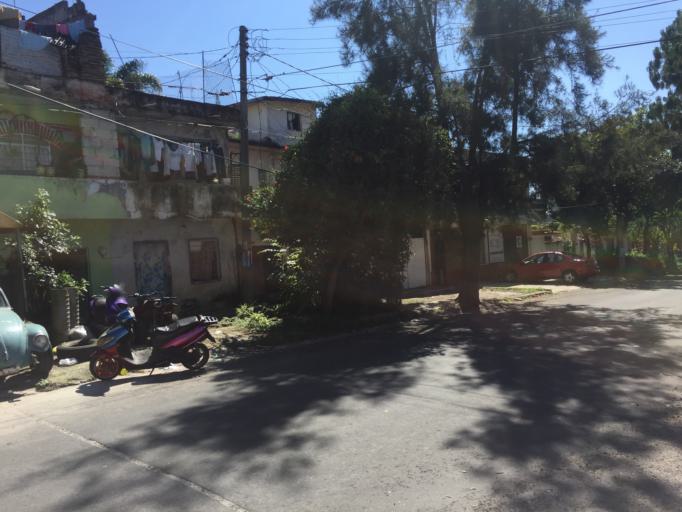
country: MX
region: Veracruz
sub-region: Xalapa
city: Xalapa de Enriquez
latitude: 19.5345
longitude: -96.9123
